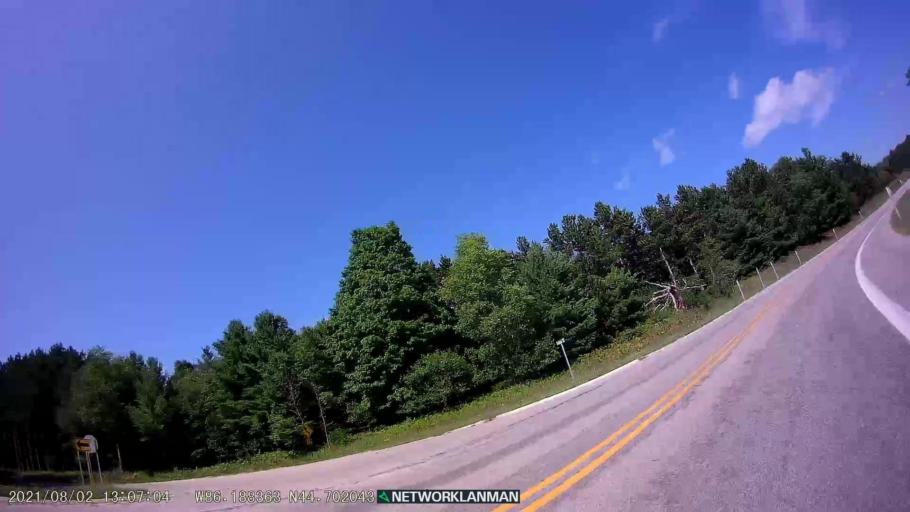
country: US
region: Michigan
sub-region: Benzie County
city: Frankfort
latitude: 44.7022
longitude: -86.1878
